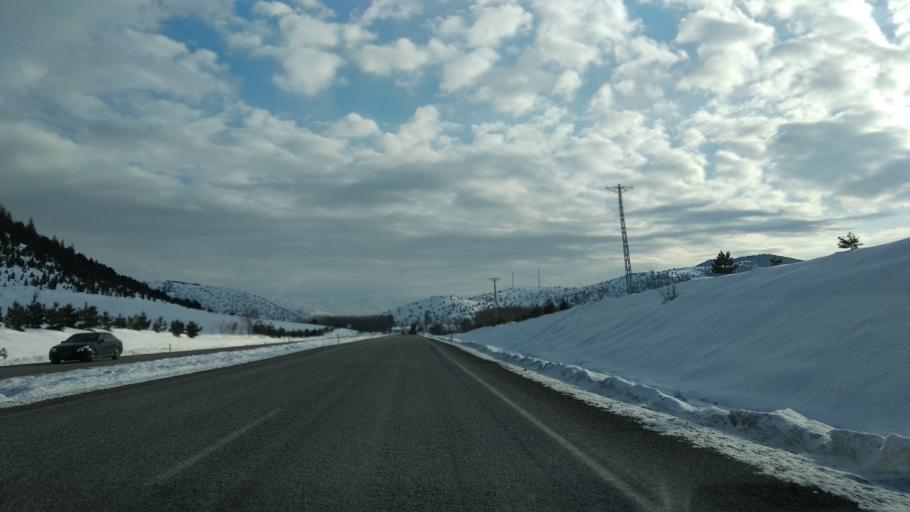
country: TR
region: Kahramanmaras
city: Goksun
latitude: 38.0750
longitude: 36.4662
